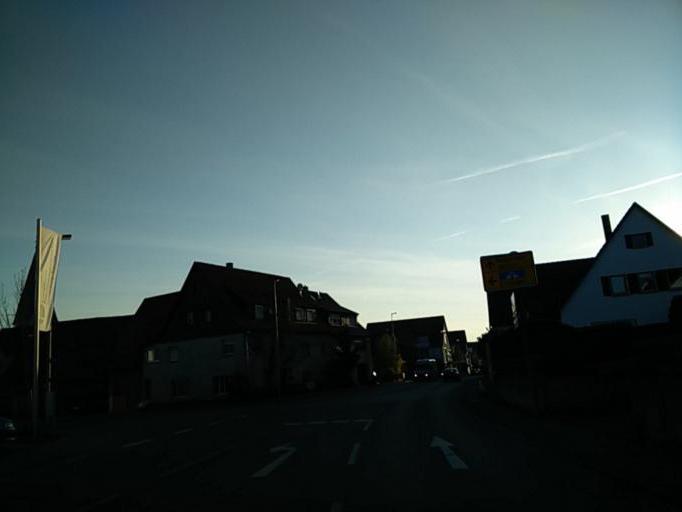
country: DE
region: Baden-Wuerttemberg
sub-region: Regierungsbezirk Stuttgart
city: Hildrizhausen
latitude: 48.6238
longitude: 8.9659
